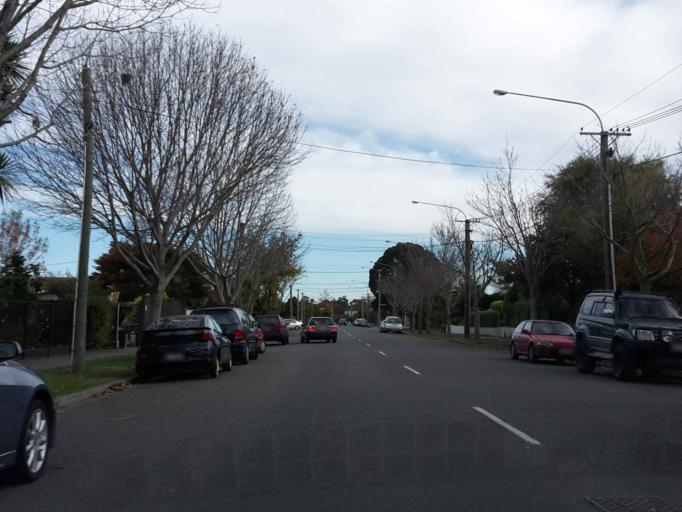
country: NZ
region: Canterbury
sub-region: Christchurch City
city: Christchurch
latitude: -43.5679
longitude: 172.6171
